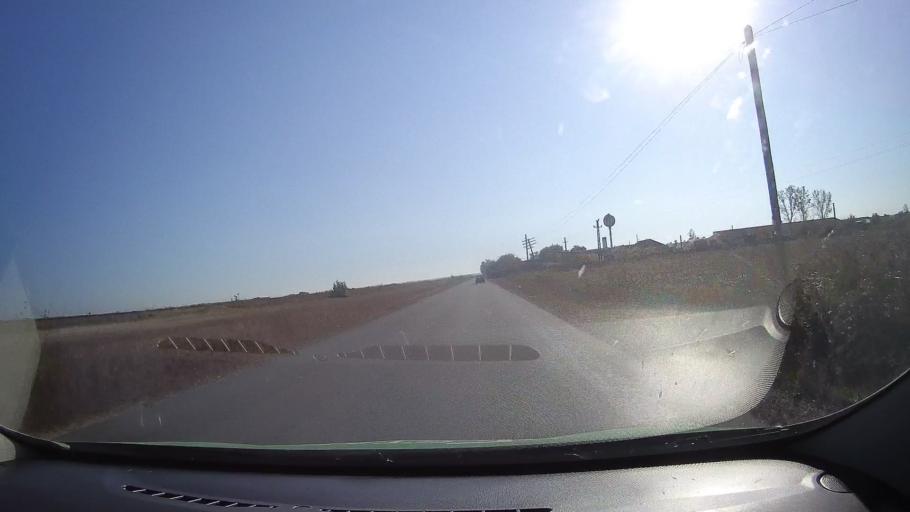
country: RO
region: Satu Mare
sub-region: Comuna Santau
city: Santau
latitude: 47.5077
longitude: 22.5244
